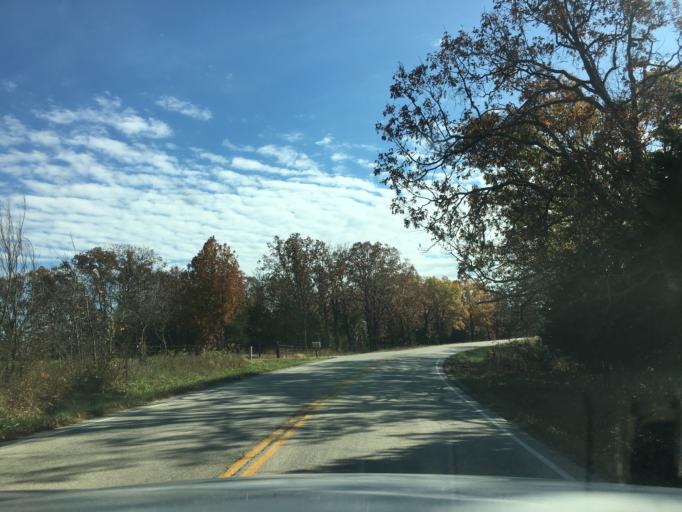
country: US
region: Missouri
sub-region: Osage County
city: Linn
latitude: 38.3701
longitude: -91.8100
